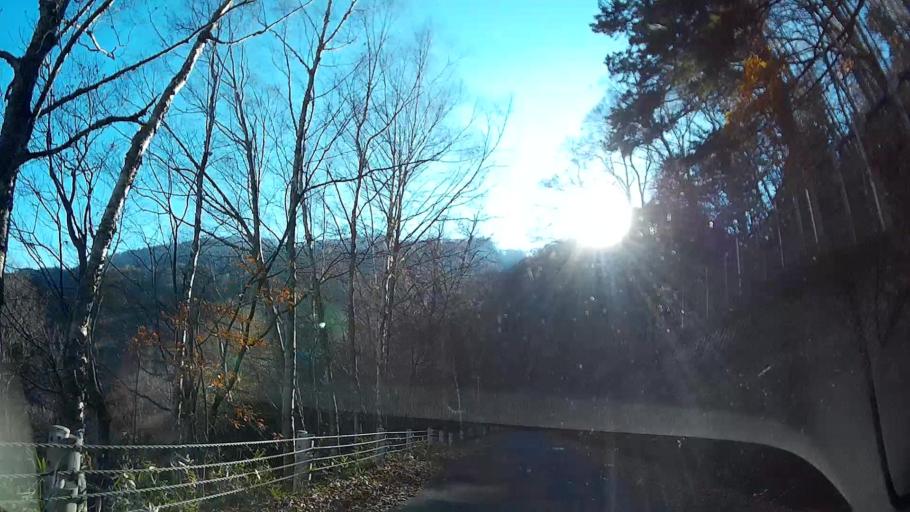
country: JP
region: Nagano
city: Hotaka
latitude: 36.2070
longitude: 137.5998
